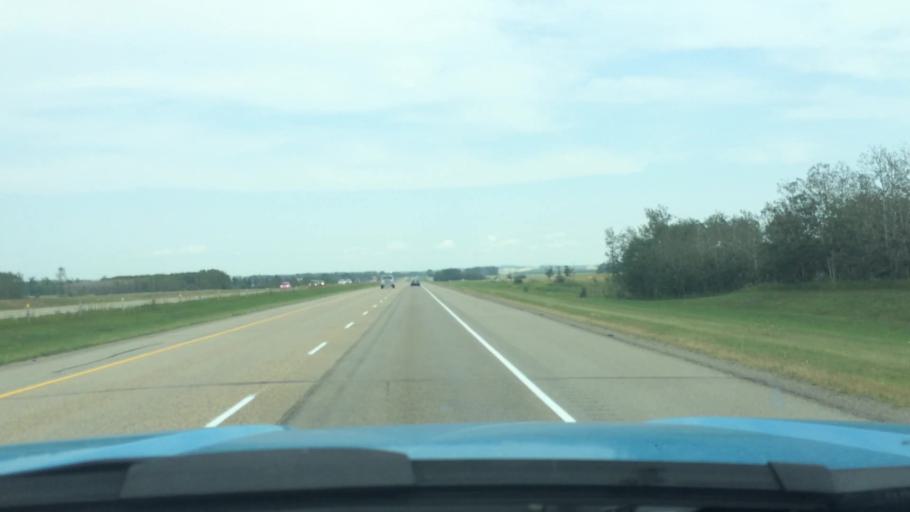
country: CA
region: Alberta
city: Olds
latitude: 51.9608
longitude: -114.0116
